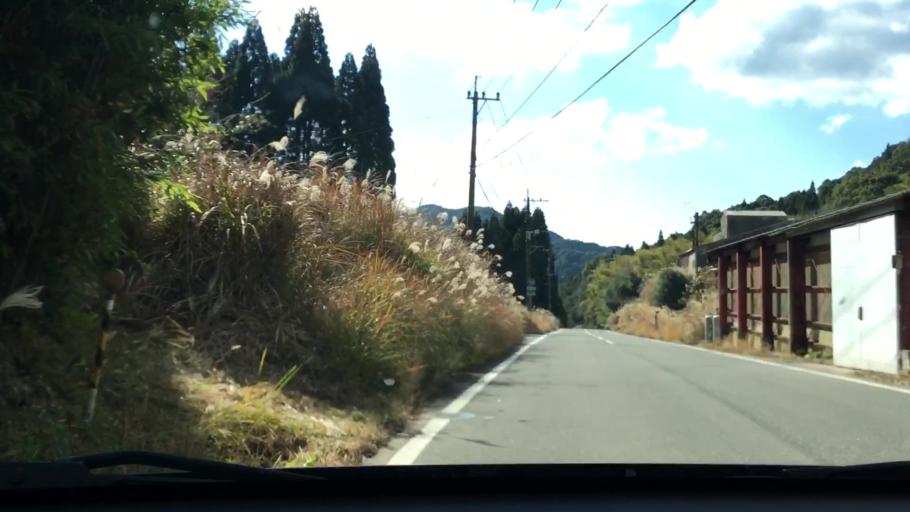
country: JP
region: Kagoshima
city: Ijuin
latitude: 31.7162
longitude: 130.4272
